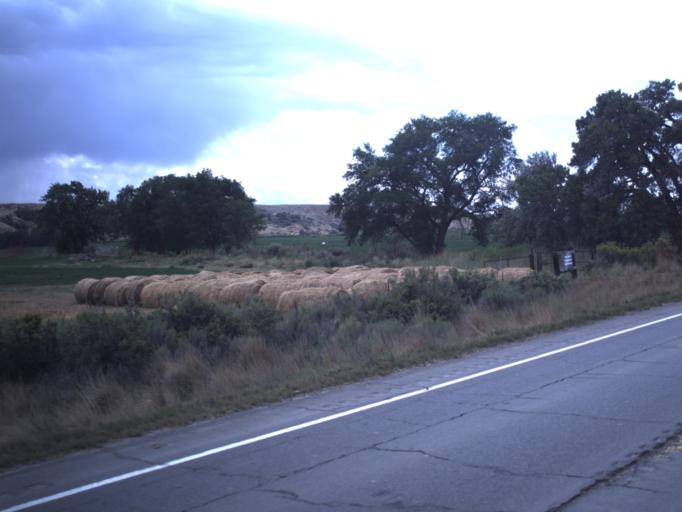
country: US
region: Utah
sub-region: Duchesne County
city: Roosevelt
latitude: 40.1731
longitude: -110.1329
